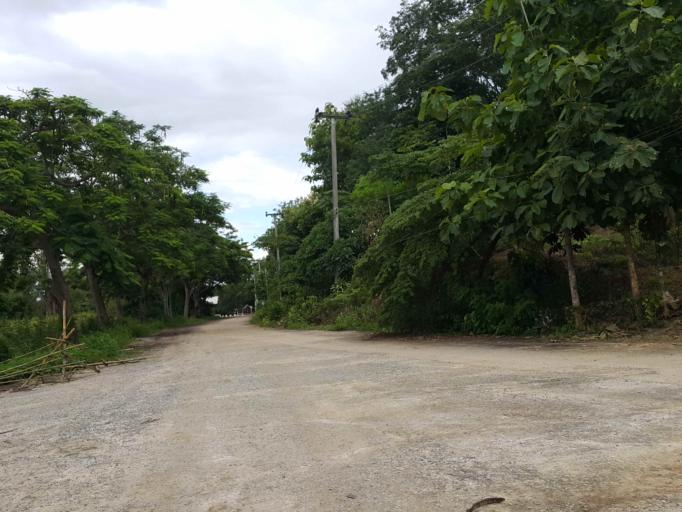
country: TH
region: Chiang Mai
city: San Sai
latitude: 18.9438
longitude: 98.9185
